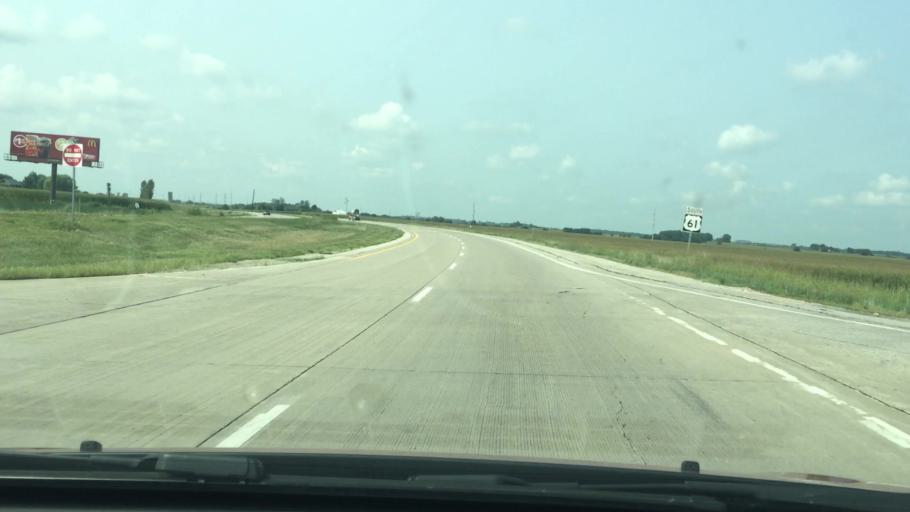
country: US
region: Iowa
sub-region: Muscatine County
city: Wilton
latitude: 41.4984
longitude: -90.9689
